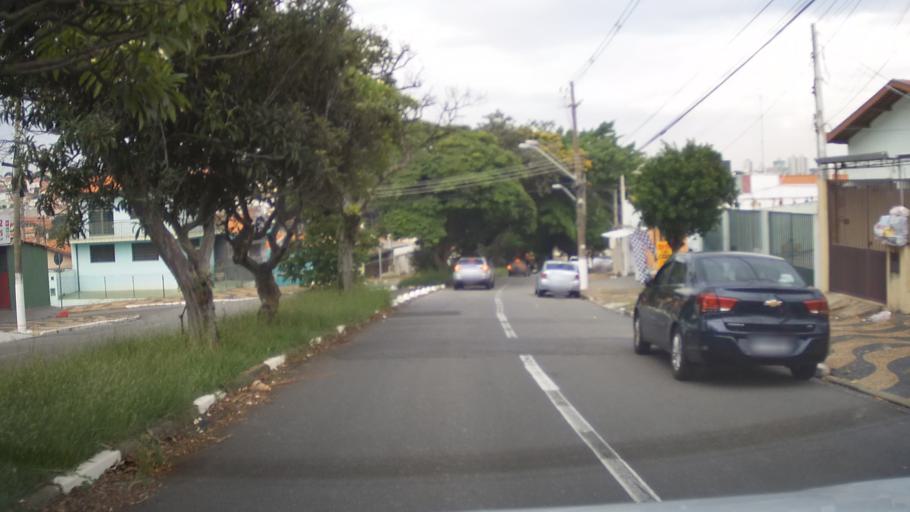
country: BR
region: Sao Paulo
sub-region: Campinas
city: Campinas
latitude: -22.9269
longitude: -47.0587
